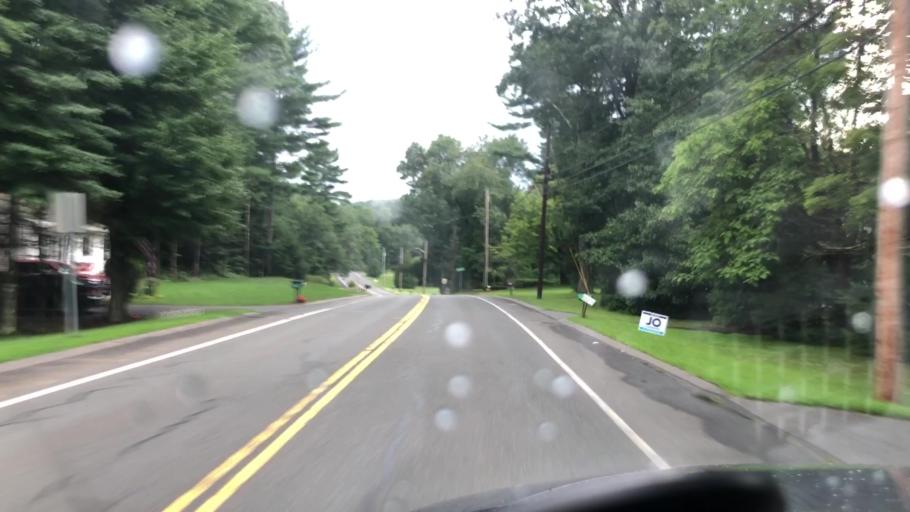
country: US
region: Massachusetts
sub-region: Hampshire County
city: Easthampton
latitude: 42.3001
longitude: -72.7119
